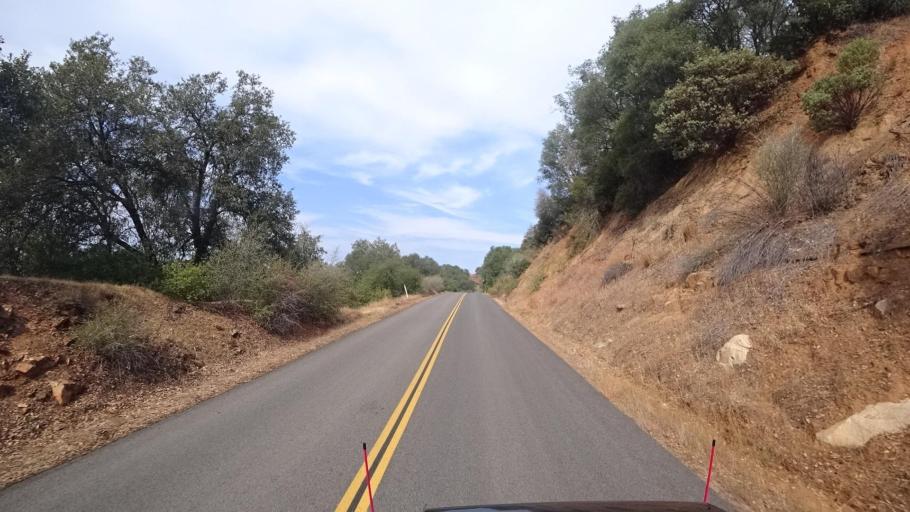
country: US
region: California
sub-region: Mariposa County
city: Midpines
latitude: 37.5125
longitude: -119.8502
